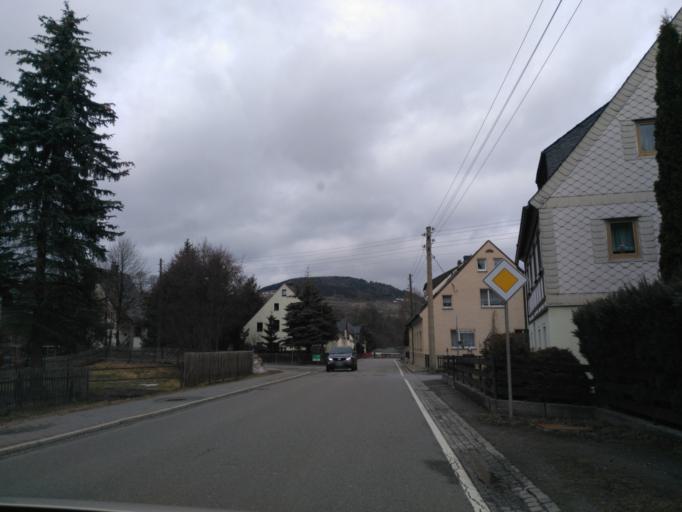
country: DE
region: Saxony
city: Konigswalde
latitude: 50.5515
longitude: 13.0452
